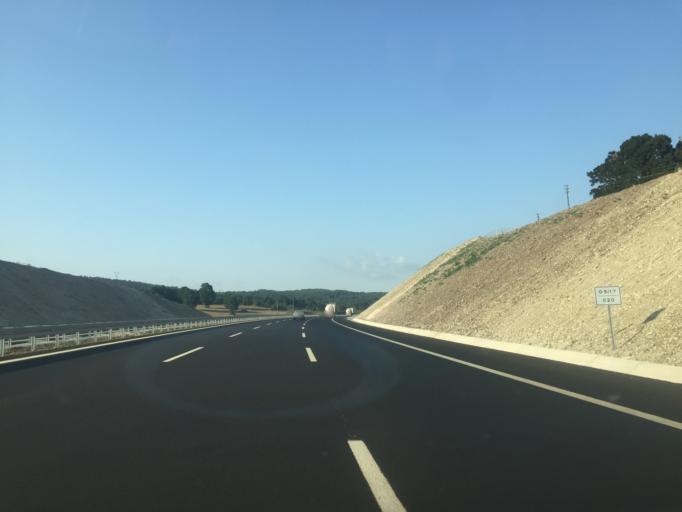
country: TR
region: Balikesir
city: Savastepe
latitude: 39.4801
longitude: 27.6507
